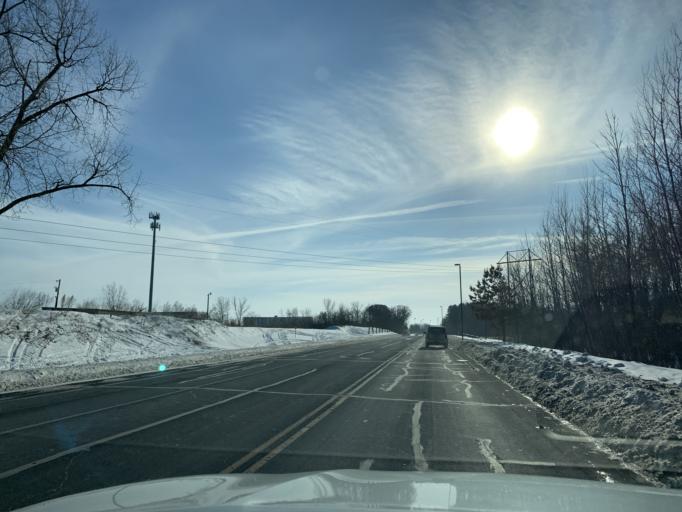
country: US
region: Minnesota
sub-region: Anoka County
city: Columbus
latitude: 45.2501
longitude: -93.0349
